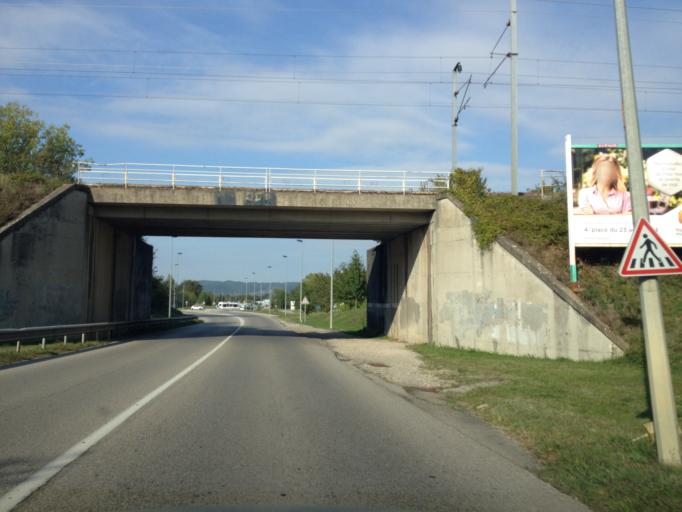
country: FR
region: Rhone-Alpes
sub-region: Departement de l'Isere
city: Villefontaine
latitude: 45.6229
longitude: 5.1621
